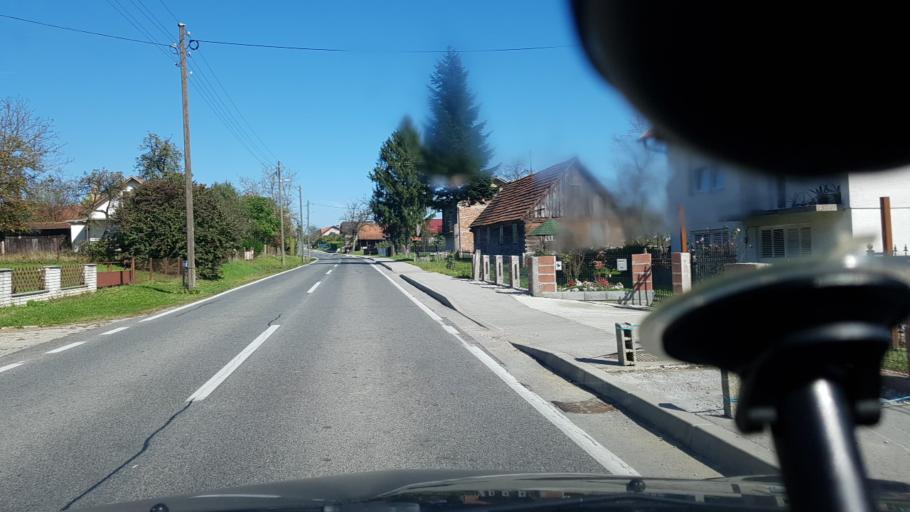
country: HR
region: Zagrebacka
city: Kriz
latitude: 45.7175
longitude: 16.4997
